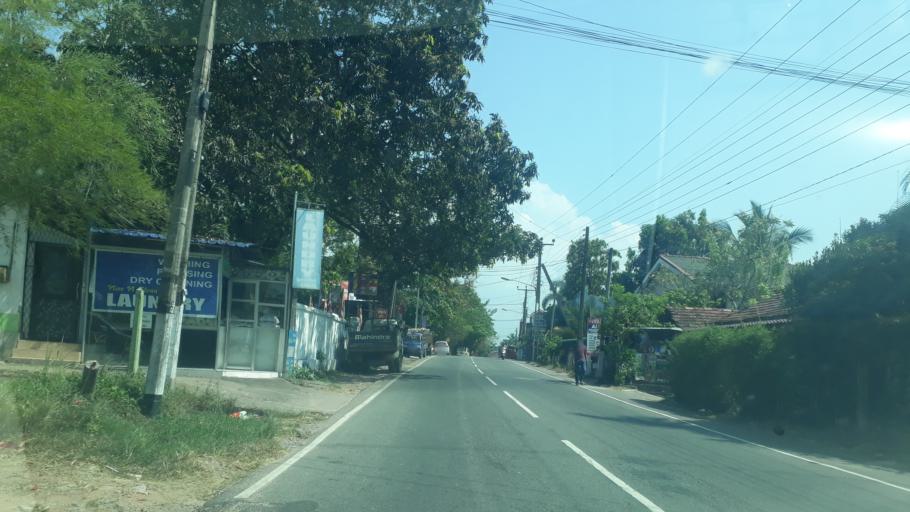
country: LK
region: Western
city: Gampaha
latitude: 7.0864
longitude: 80.0080
